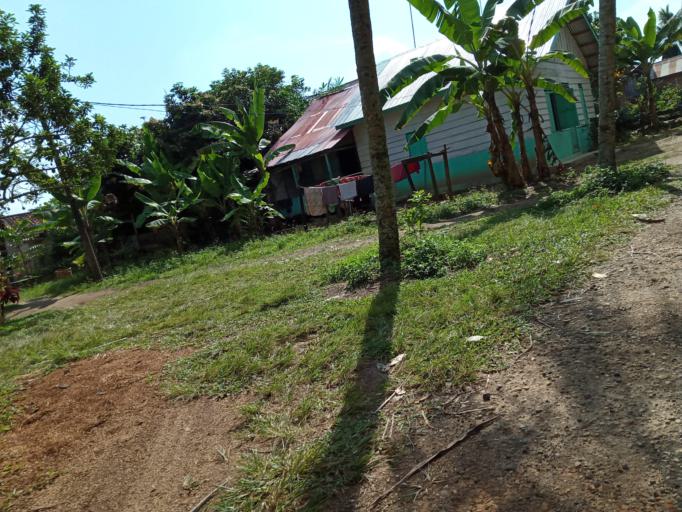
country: ID
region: Jambi
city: Muara Bulian
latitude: -1.6456
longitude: 103.2836
